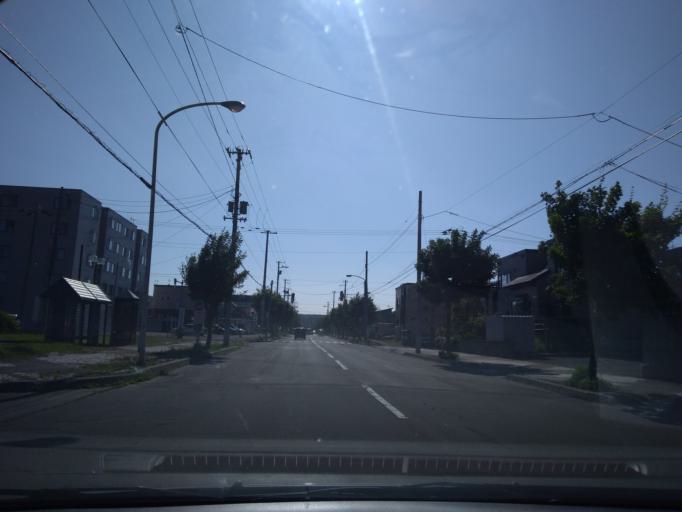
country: JP
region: Hokkaido
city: Kitahiroshima
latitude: 42.9878
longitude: 141.5728
